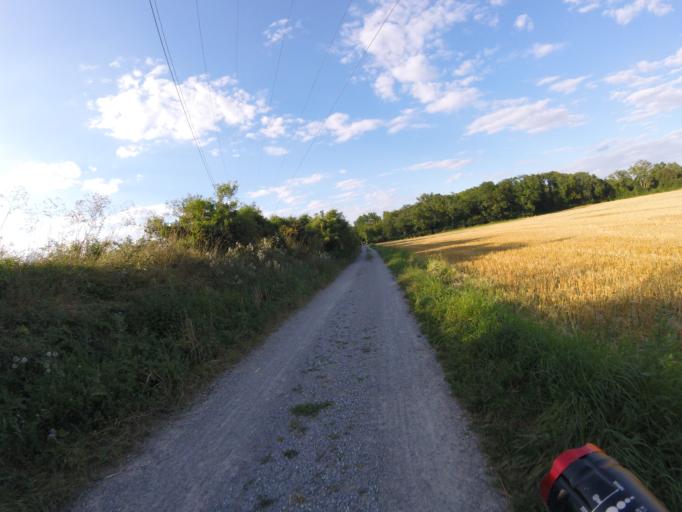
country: AT
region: Lower Austria
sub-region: Politischer Bezirk Modling
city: Munchendorf
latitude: 48.0185
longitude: 16.3709
